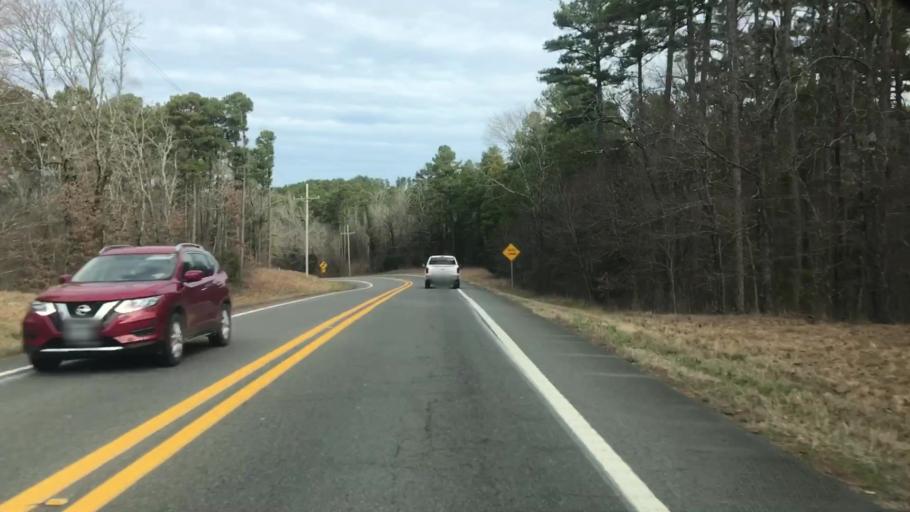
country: US
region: Arkansas
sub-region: Montgomery County
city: Mount Ida
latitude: 34.5900
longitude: -93.6643
